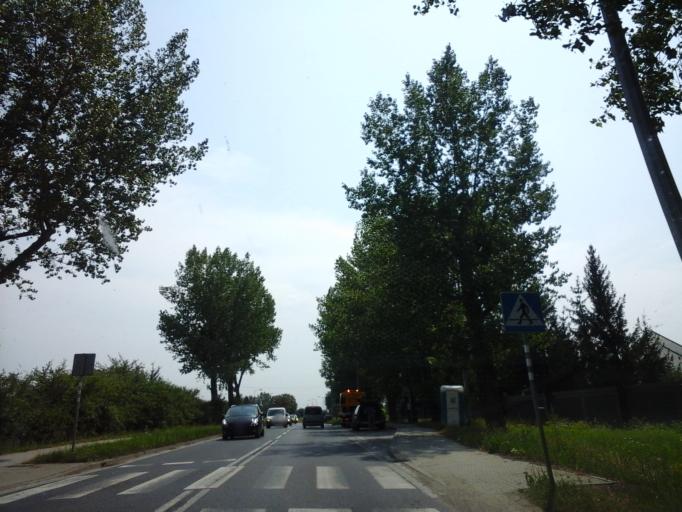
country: PL
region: Lower Silesian Voivodeship
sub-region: Powiat wroclawski
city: Zerniki Wroclawskie
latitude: 51.0450
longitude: 17.0608
